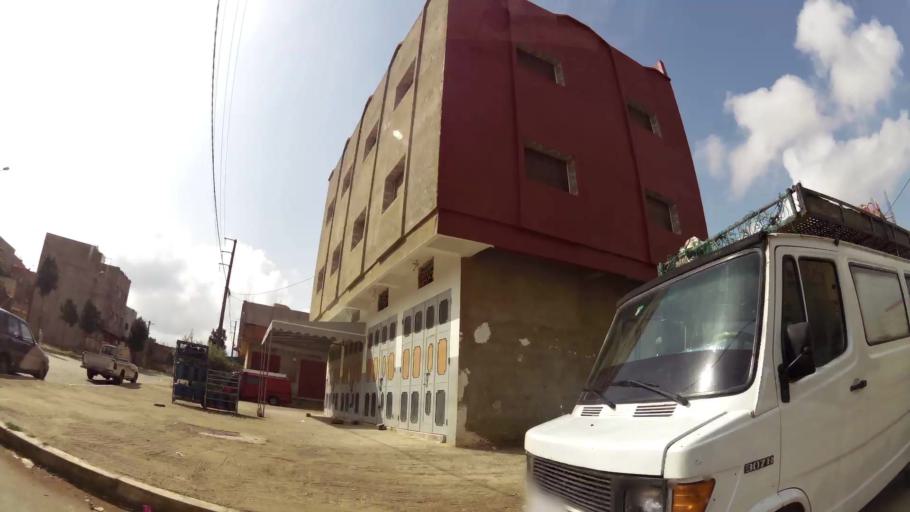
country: MA
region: Rabat-Sale-Zemmour-Zaer
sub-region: Khemisset
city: Tiflet
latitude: 33.9006
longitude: -6.3177
